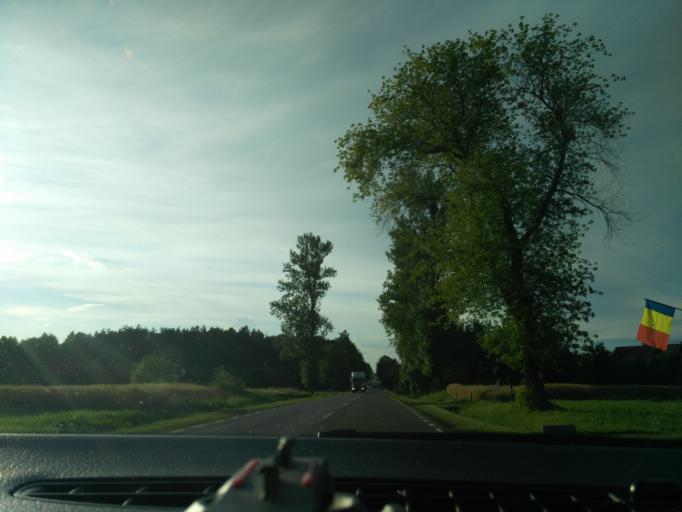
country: PL
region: Lublin Voivodeship
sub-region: Powiat krasnicki
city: Szastarka
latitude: 50.8683
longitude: 22.2732
